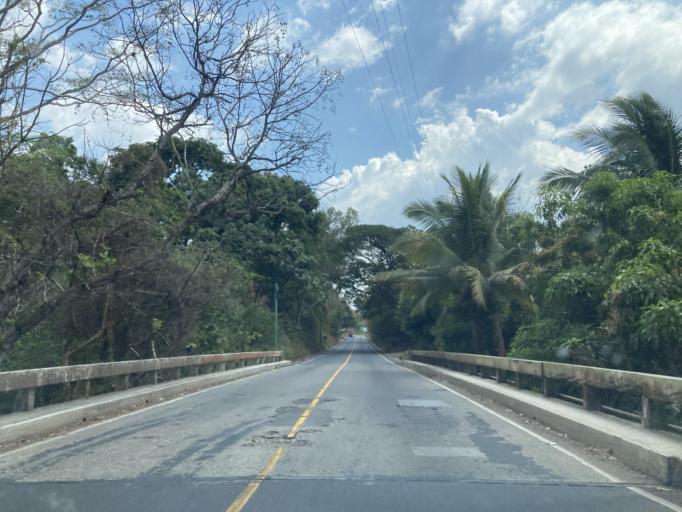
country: GT
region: Santa Rosa
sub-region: Municipio de Taxisco
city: Taxisco
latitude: 14.0650
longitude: -90.4557
